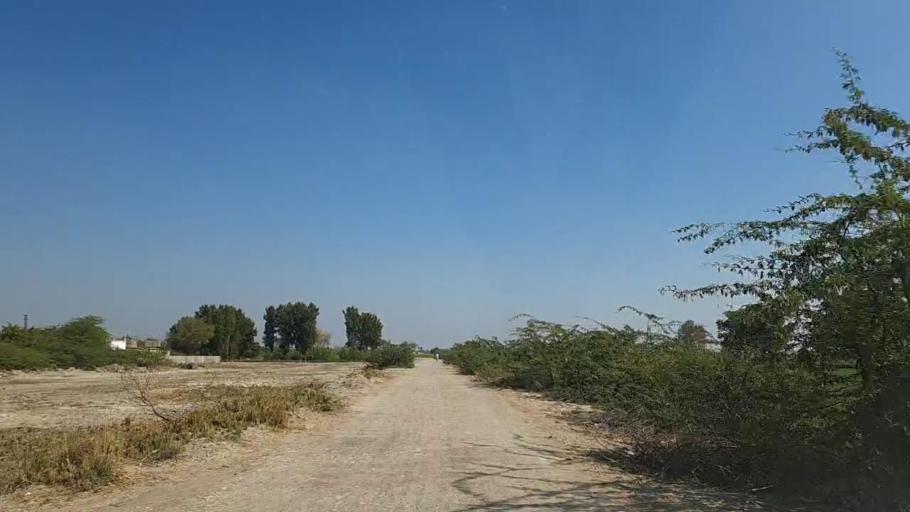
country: PK
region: Sindh
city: Nawabshah
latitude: 26.2557
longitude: 68.4416
